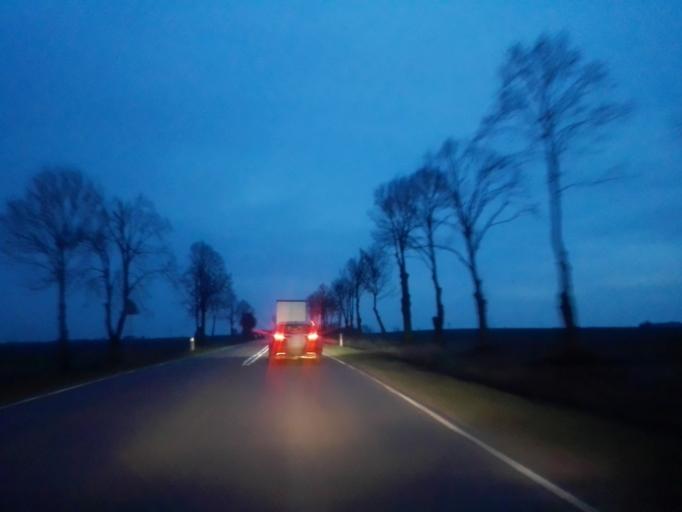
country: PL
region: Podlasie
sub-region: Lomza
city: Lomza
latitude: 53.1221
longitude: 22.0334
